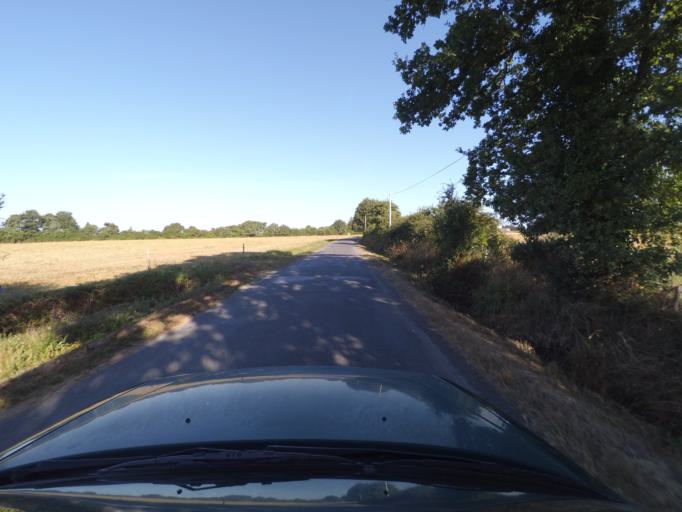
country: FR
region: Pays de la Loire
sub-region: Departement de la Loire-Atlantique
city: Le Bignon
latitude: 47.0914
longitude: -1.4797
